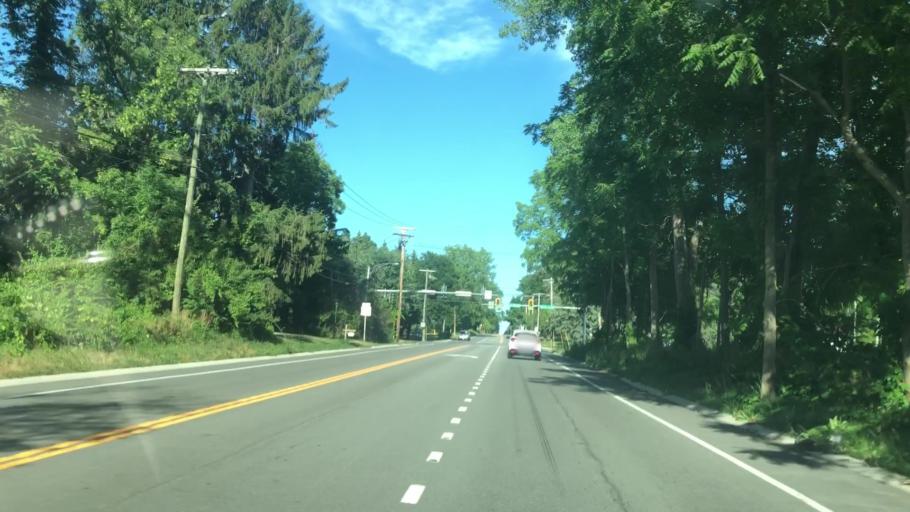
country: US
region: New York
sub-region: Monroe County
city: Fairport
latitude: 43.1305
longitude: -77.4017
